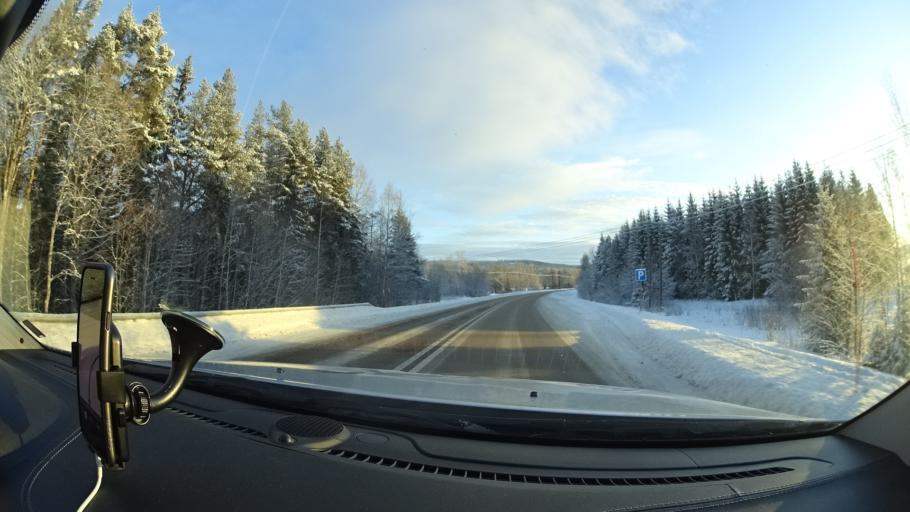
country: SE
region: Jaemtland
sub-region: Ragunda Kommun
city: Hammarstrand
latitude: 63.1801
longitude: 15.9382
